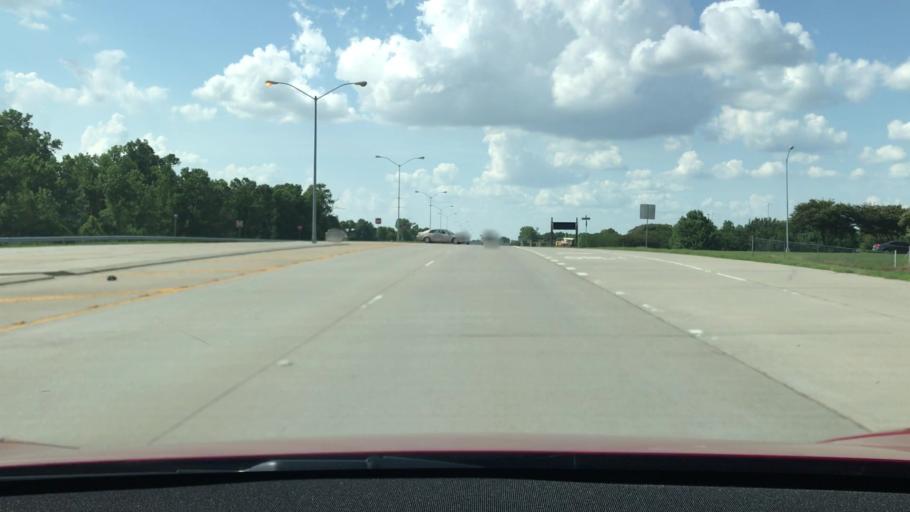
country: US
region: Louisiana
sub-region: Bossier Parish
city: Bossier City
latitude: 32.4615
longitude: -93.6757
